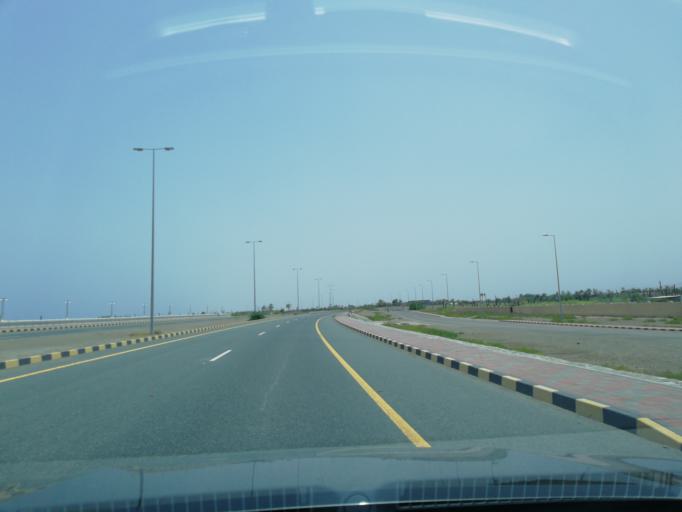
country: OM
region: Al Batinah
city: Shinas
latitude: 24.8419
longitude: 56.4254
